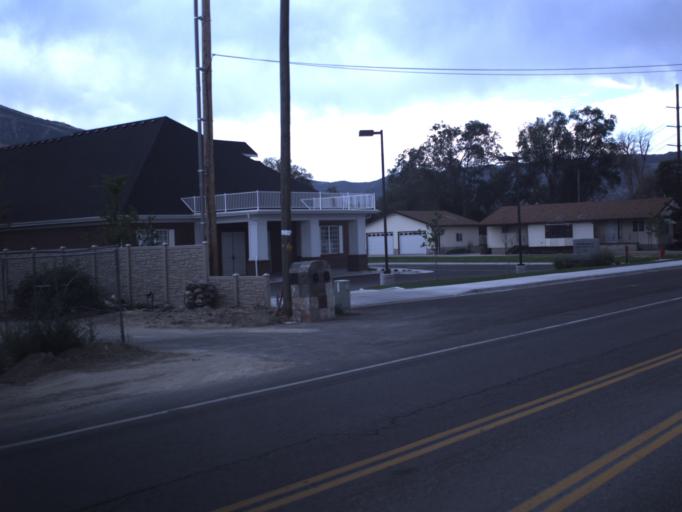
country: US
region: Utah
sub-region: Salt Lake County
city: Draper
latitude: 40.5360
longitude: -111.8712
